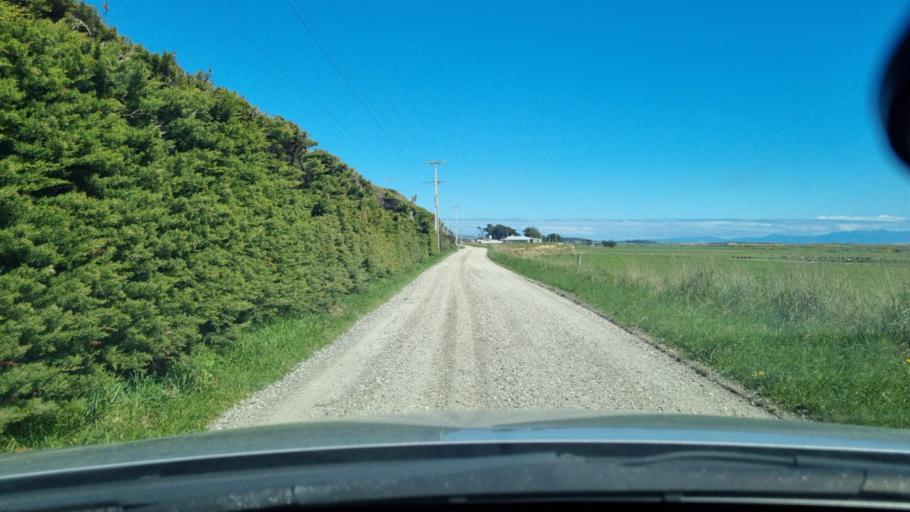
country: NZ
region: Southland
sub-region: Invercargill City
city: Invercargill
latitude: -46.3944
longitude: 168.2578
